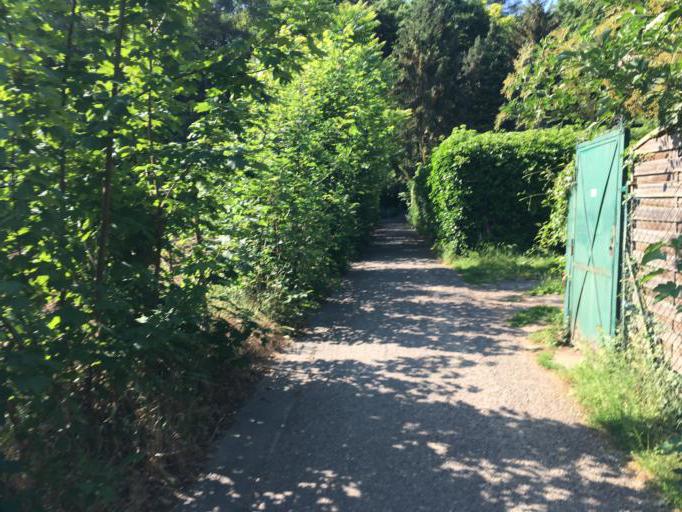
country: DE
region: Hesse
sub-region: Regierungsbezirk Darmstadt
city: Frankfurt am Main
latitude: 50.0903
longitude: 8.7196
